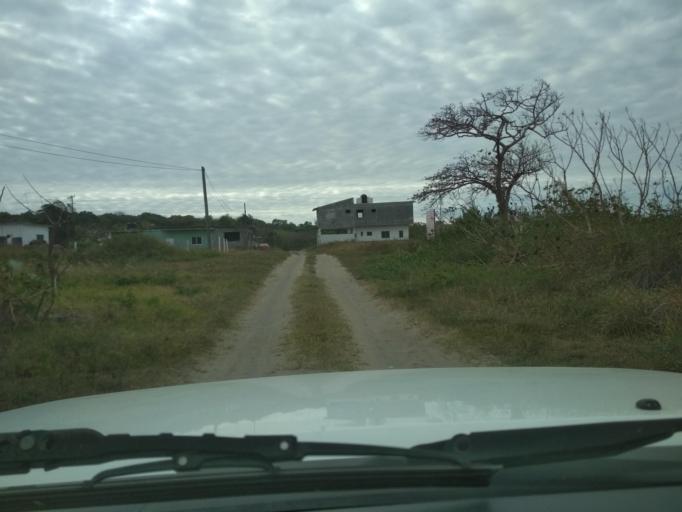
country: MX
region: Veracruz
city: Anton Lizardo
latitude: 19.0526
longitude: -95.9889
